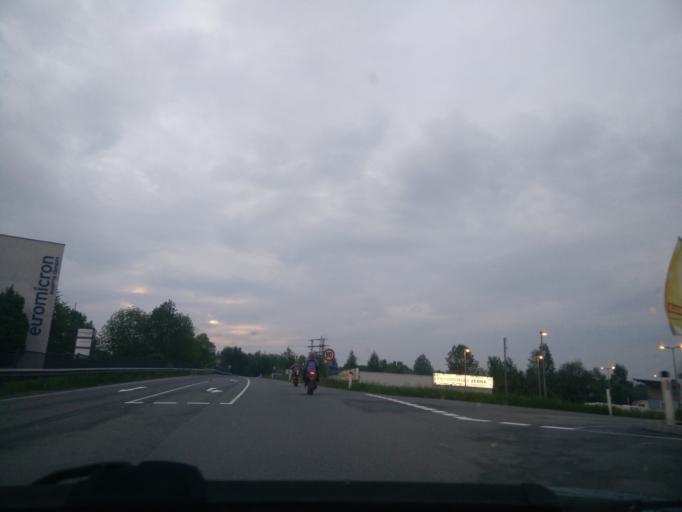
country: AT
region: Salzburg
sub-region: Politischer Bezirk Salzburg-Umgebung
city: Seekirchen am Wallersee
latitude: 47.8884
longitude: 13.1212
